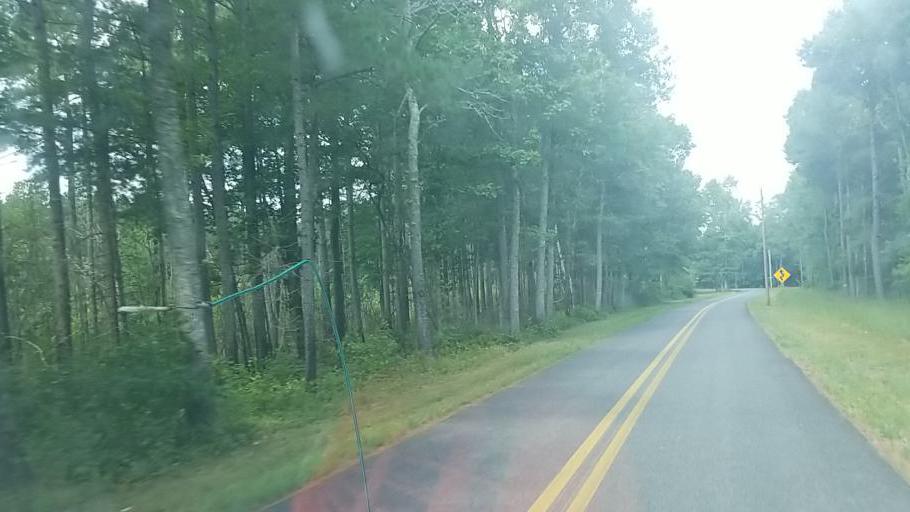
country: US
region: Maryland
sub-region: Worcester County
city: Snow Hill
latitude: 38.2539
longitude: -75.4361
